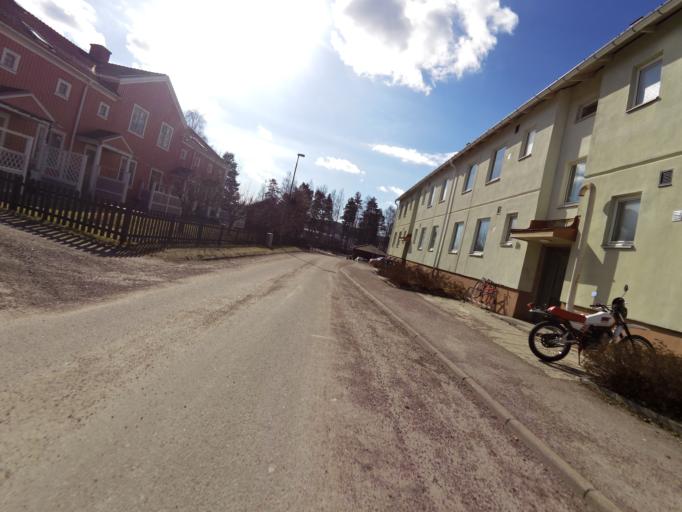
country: SE
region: Gaevleborg
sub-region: Hofors Kommun
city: Hofors
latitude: 60.5437
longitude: 16.2914
